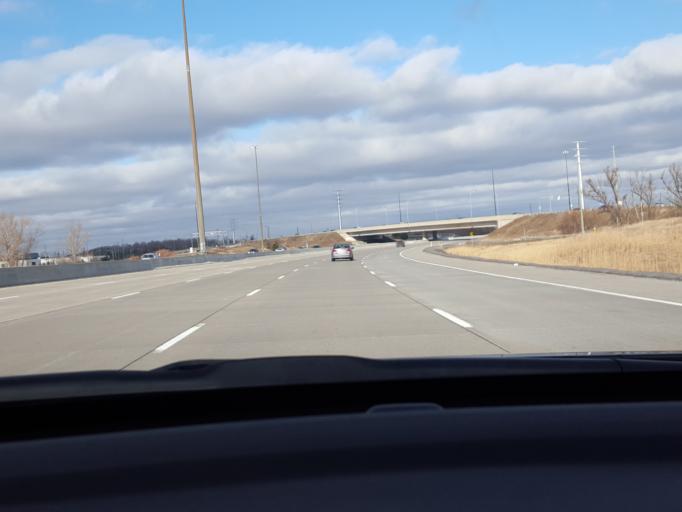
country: CA
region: Ontario
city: Concord
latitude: 43.8145
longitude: -79.4791
